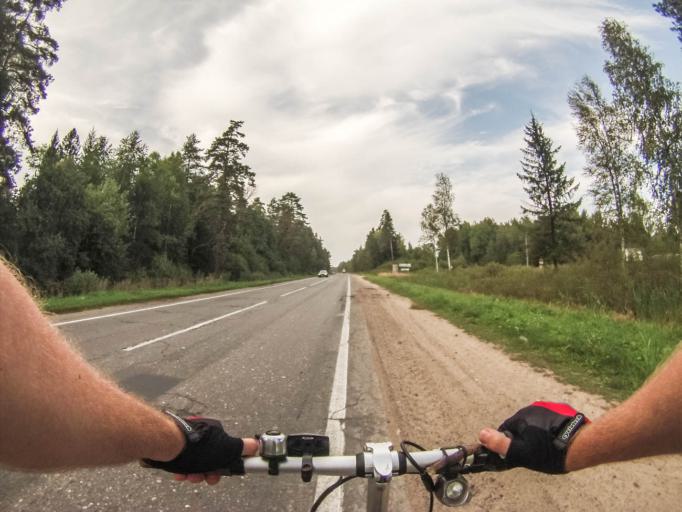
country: RU
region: Jaroslavl
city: Uglich
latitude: 57.4943
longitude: 38.3516
